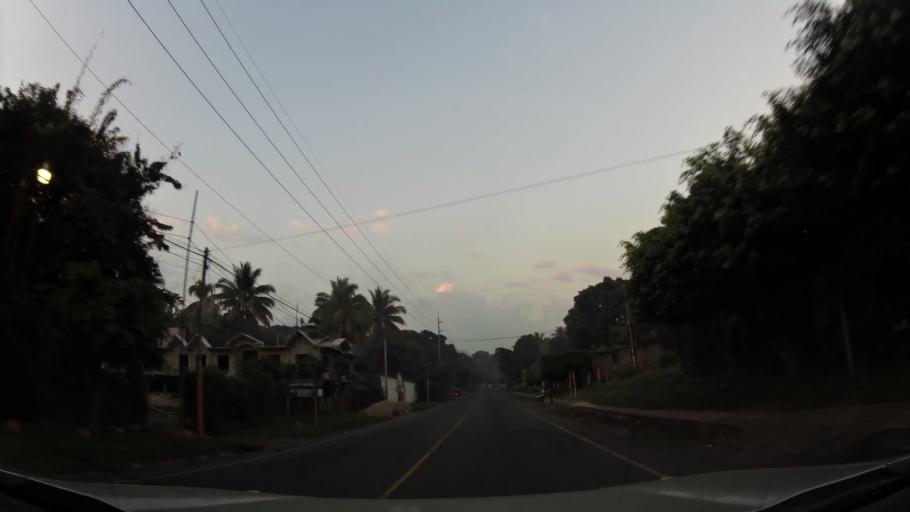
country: GT
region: Retalhuleu
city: Santa Cruz Mulua
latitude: 14.5872
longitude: -91.6218
